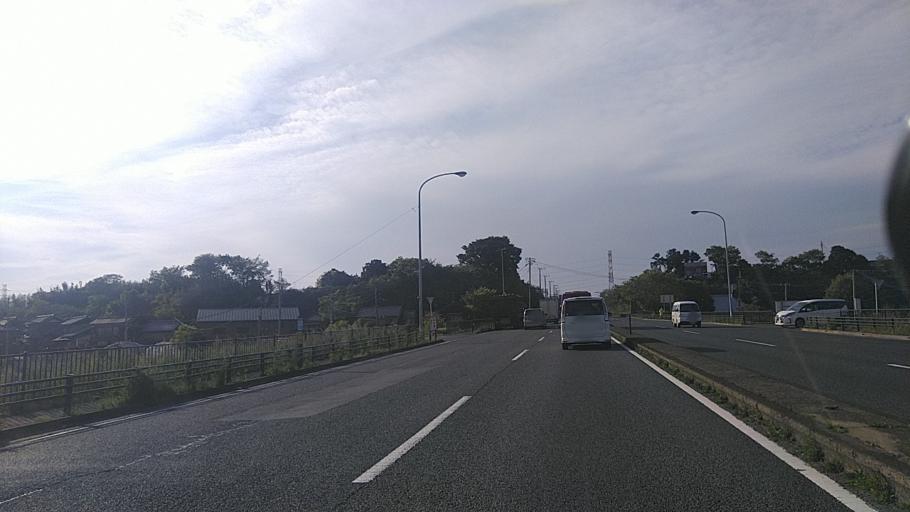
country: JP
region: Chiba
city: Shiroi
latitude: 35.7607
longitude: 140.1049
